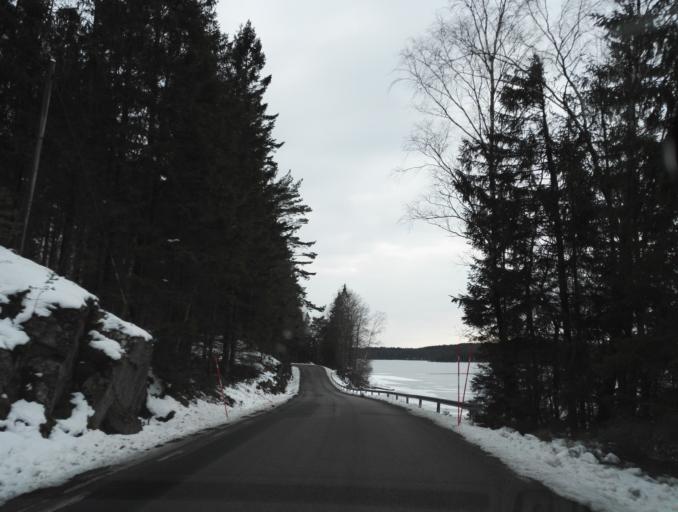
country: SE
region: Vaestra Goetaland
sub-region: Alingsas Kommun
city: Ingared
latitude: 57.7758
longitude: 12.4958
